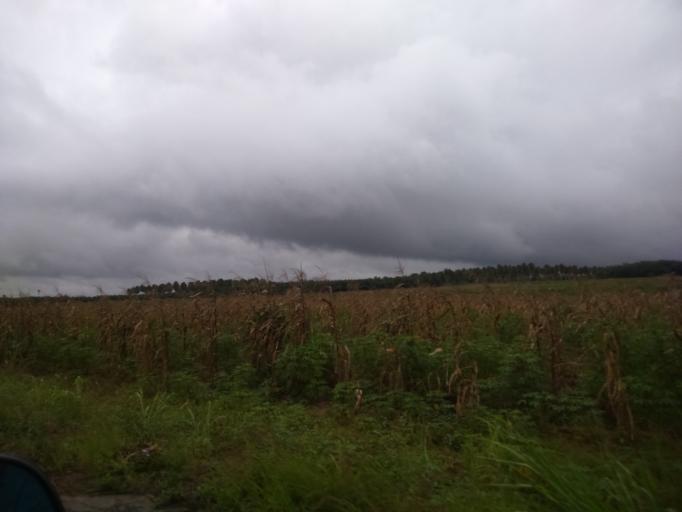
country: CI
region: Sud-Comoe
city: Adiake
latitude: 5.3007
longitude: -3.3543
